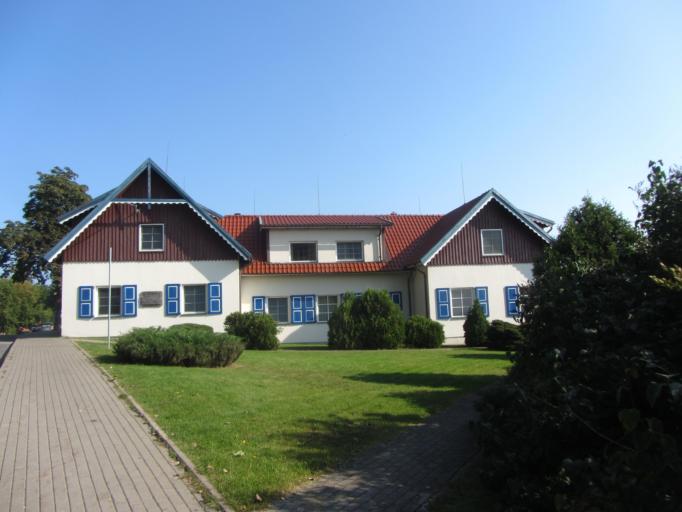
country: LT
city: Nida
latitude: 55.3102
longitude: 21.0099
